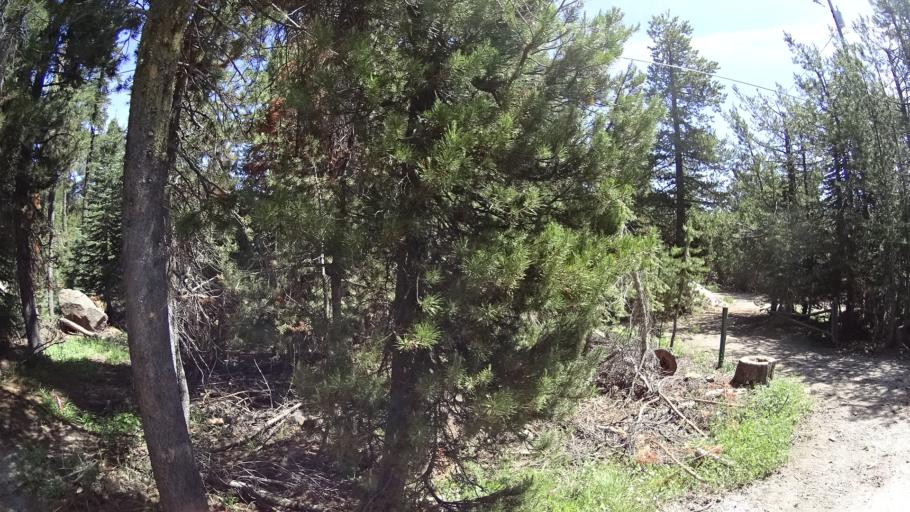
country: US
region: California
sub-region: Calaveras County
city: Arnold
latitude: 38.4462
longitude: -120.0680
